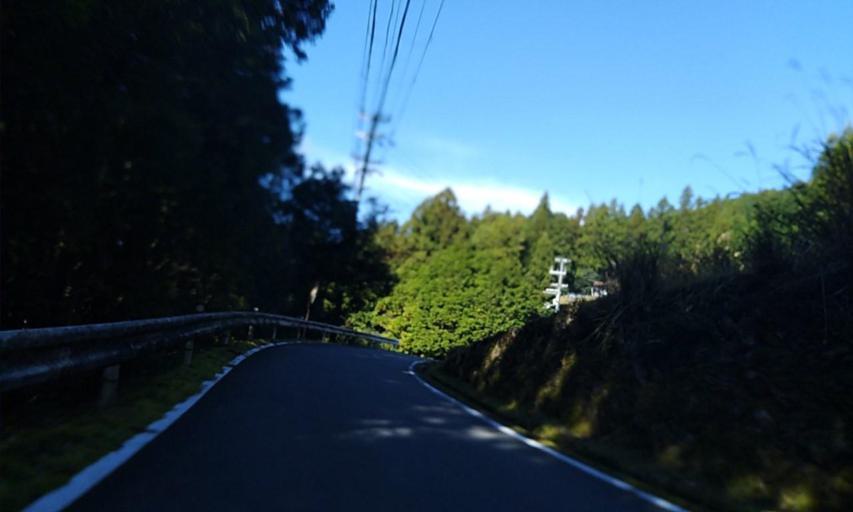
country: JP
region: Wakayama
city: Shingu
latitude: 33.9327
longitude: 135.9789
